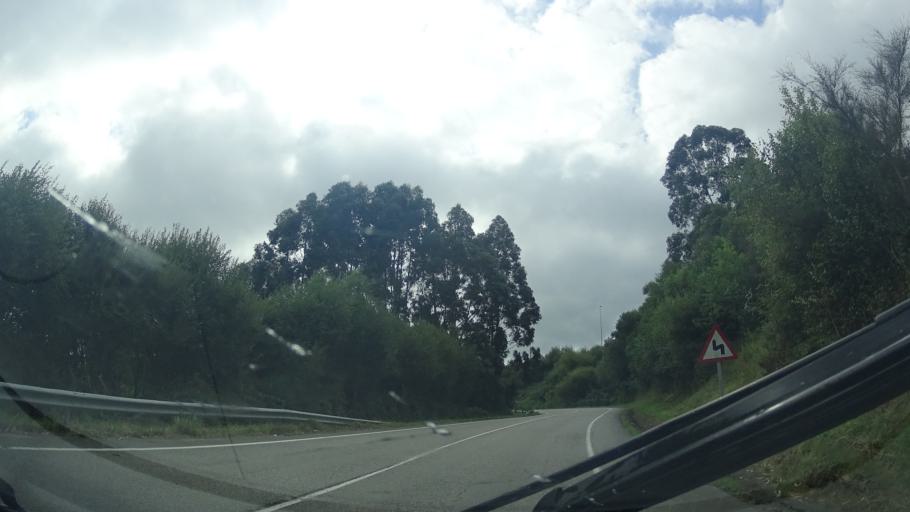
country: ES
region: Asturias
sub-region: Province of Asturias
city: Ribadesella
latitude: 43.4605
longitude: -5.1184
